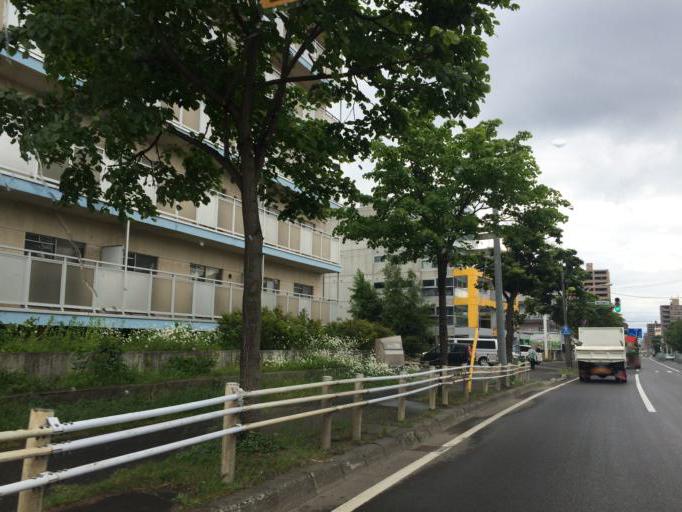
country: JP
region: Hokkaido
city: Sapporo
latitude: 43.0280
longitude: 141.3380
